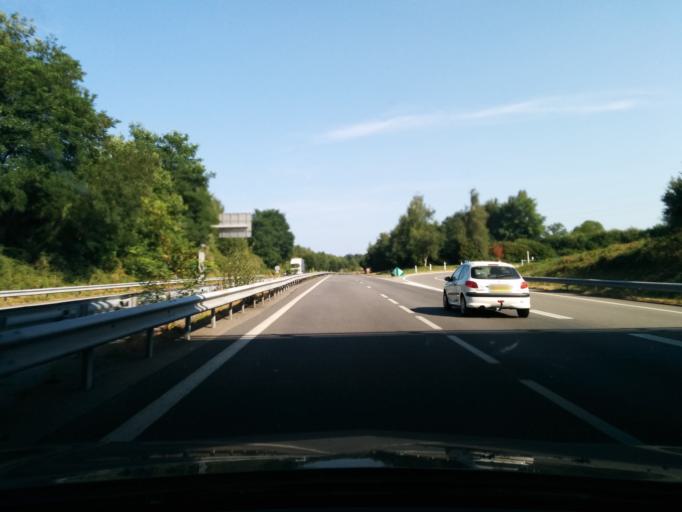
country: FR
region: Limousin
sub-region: Departement de la Haute-Vienne
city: Saint-Germain-les-Belles
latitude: 45.6255
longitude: 1.4408
